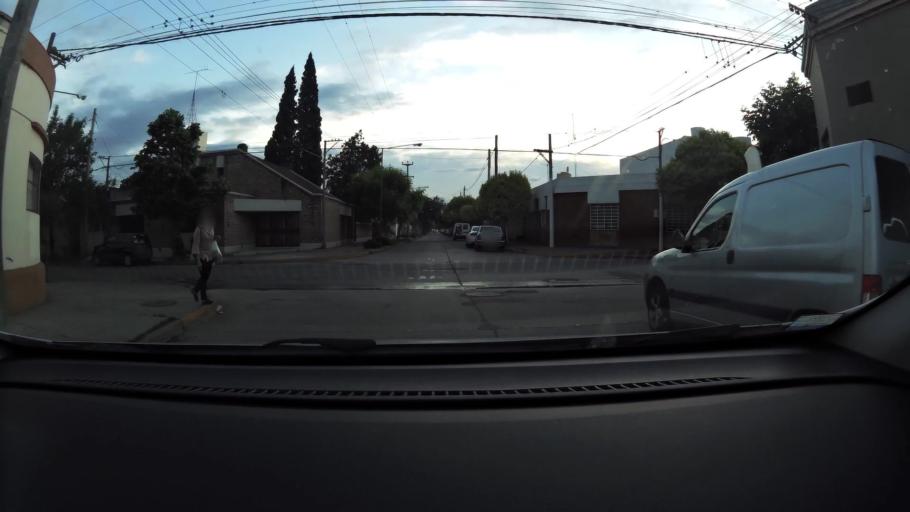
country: AR
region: Buenos Aires
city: San Nicolas de los Arroyos
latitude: -33.3255
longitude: -60.2257
